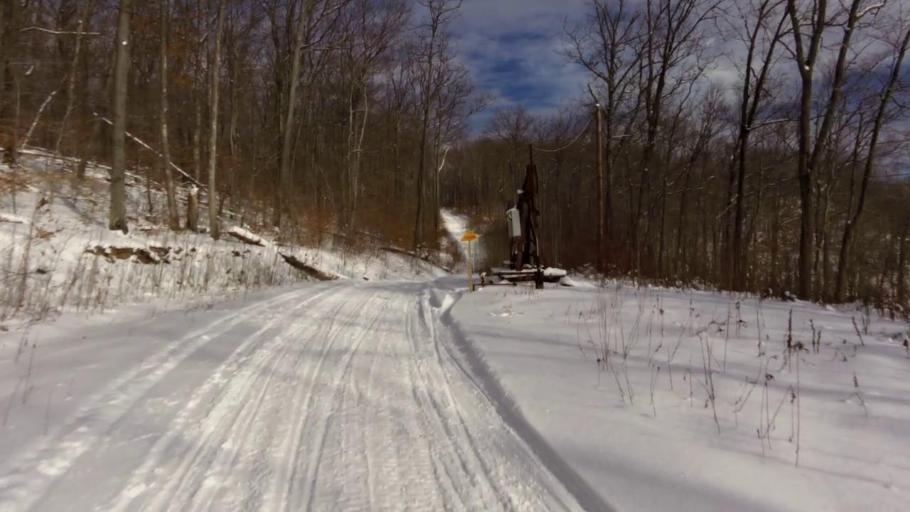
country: US
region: Pennsylvania
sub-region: McKean County
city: Foster Brook
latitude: 42.0064
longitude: -78.5936
